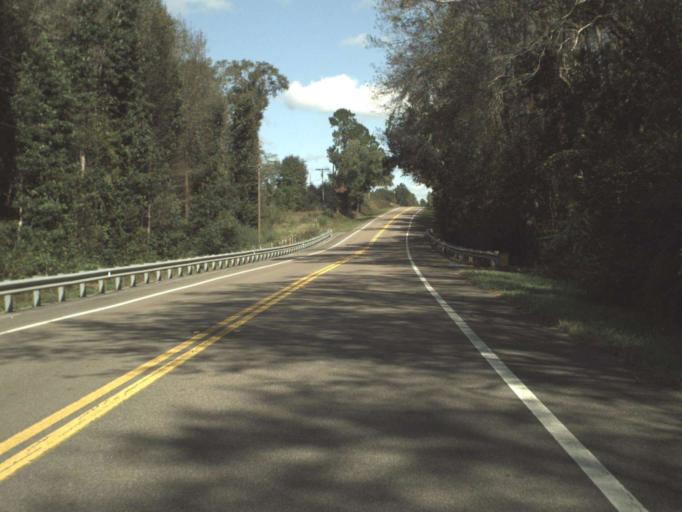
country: US
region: Alabama
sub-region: Covington County
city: Florala
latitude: 30.9267
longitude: -86.1373
